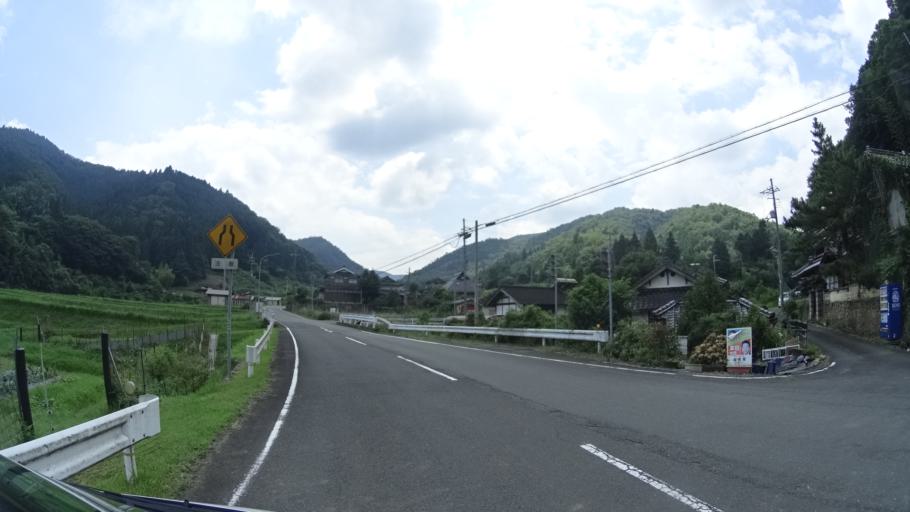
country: JP
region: Kyoto
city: Ayabe
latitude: 35.1934
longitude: 135.2167
